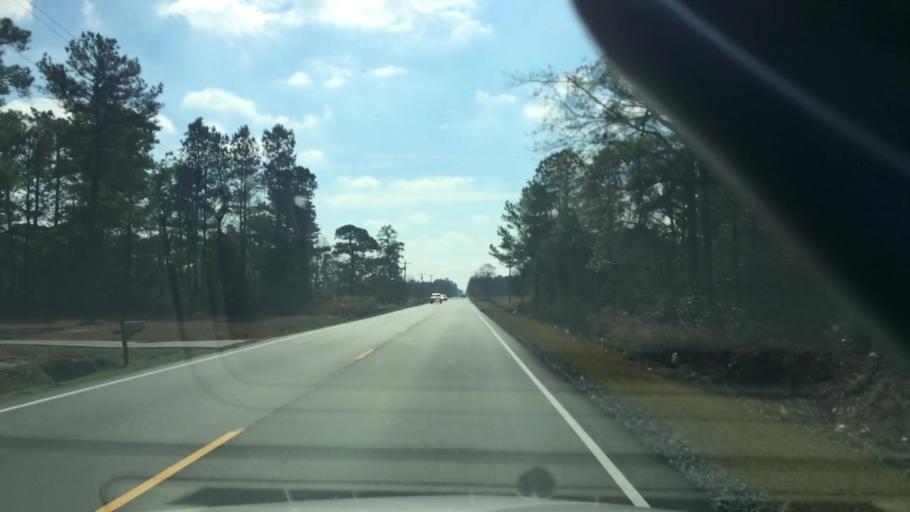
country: US
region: North Carolina
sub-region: Duplin County
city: Beulaville
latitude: 35.0238
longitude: -77.7495
